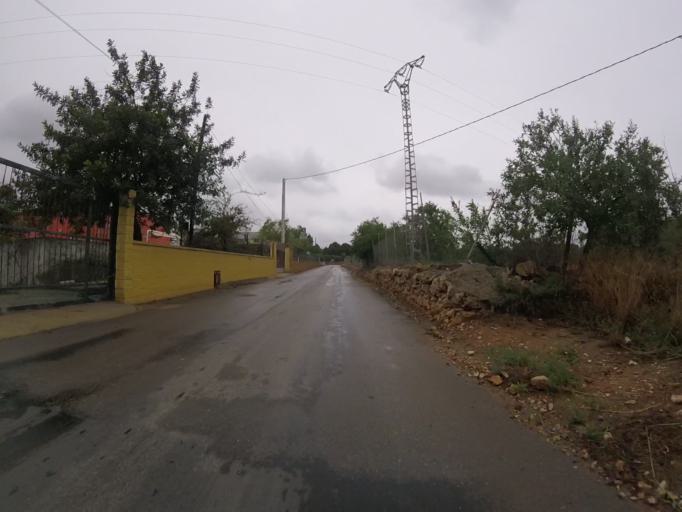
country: ES
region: Valencia
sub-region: Provincia de Castello
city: Alcoceber
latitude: 40.2481
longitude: 0.2462
